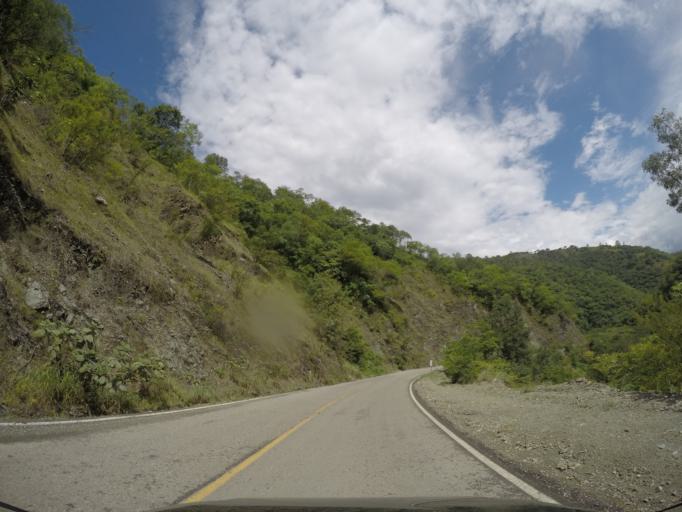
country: MX
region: Oaxaca
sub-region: San Jeronimo Coatlan
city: San Cristobal Honduras
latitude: 16.3674
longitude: -97.0885
